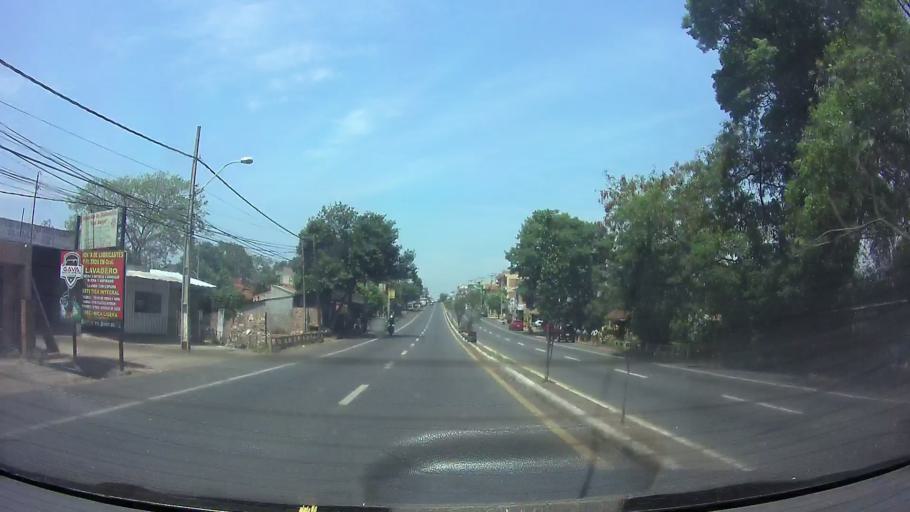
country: PY
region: Central
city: Itaugua
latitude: -25.3898
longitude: -57.3596
